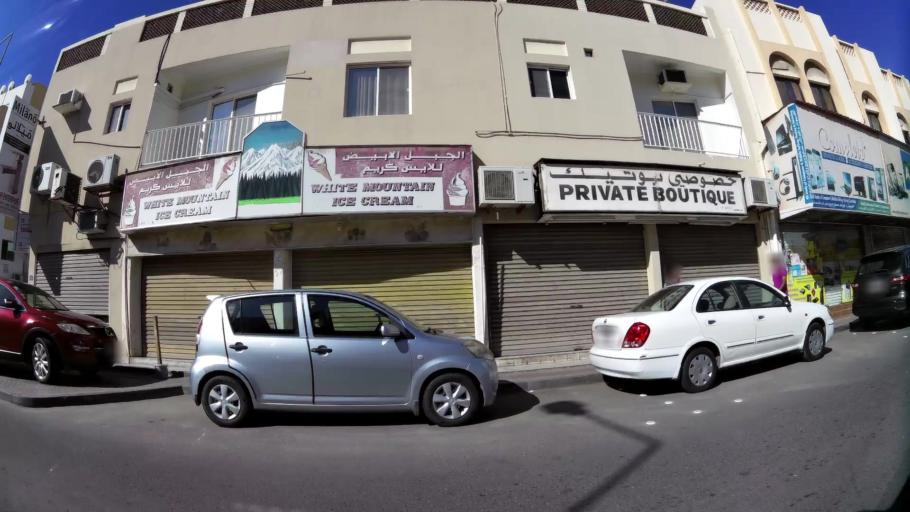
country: BH
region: Muharraq
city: Al Muharraq
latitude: 26.2581
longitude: 50.6166
